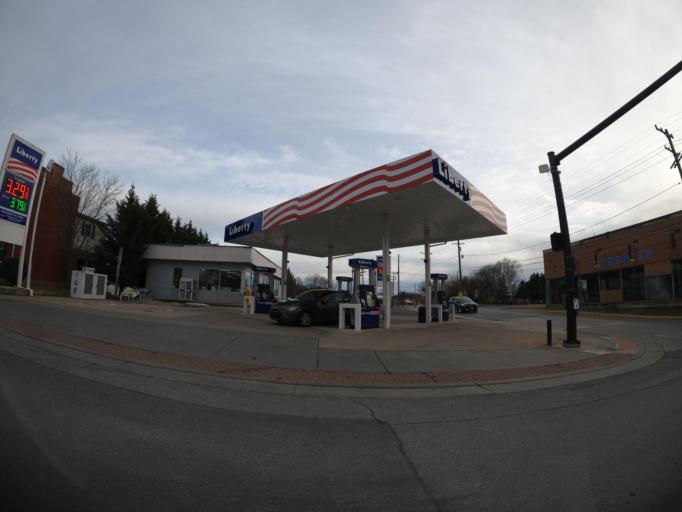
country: US
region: West Virginia
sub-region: Jefferson County
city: Charles Town
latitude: 39.2876
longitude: -77.8628
